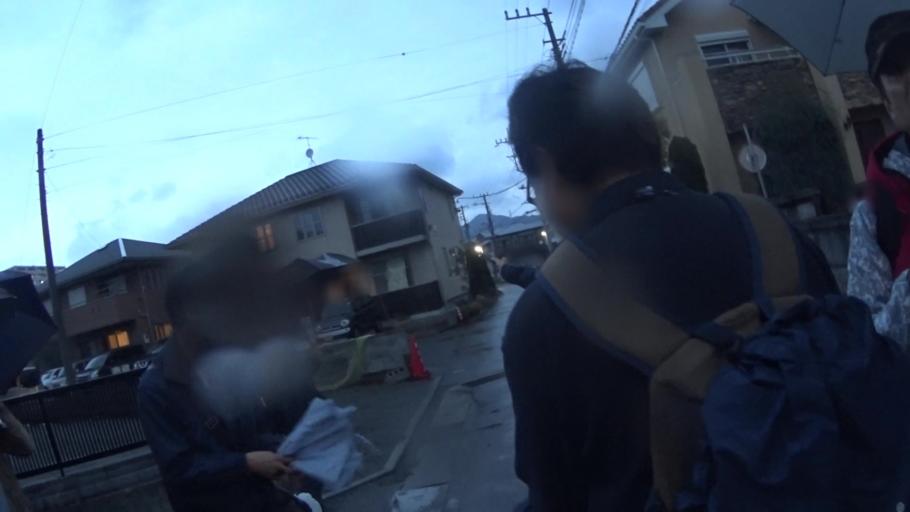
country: JP
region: Kanagawa
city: Hadano
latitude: 35.3691
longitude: 139.2283
